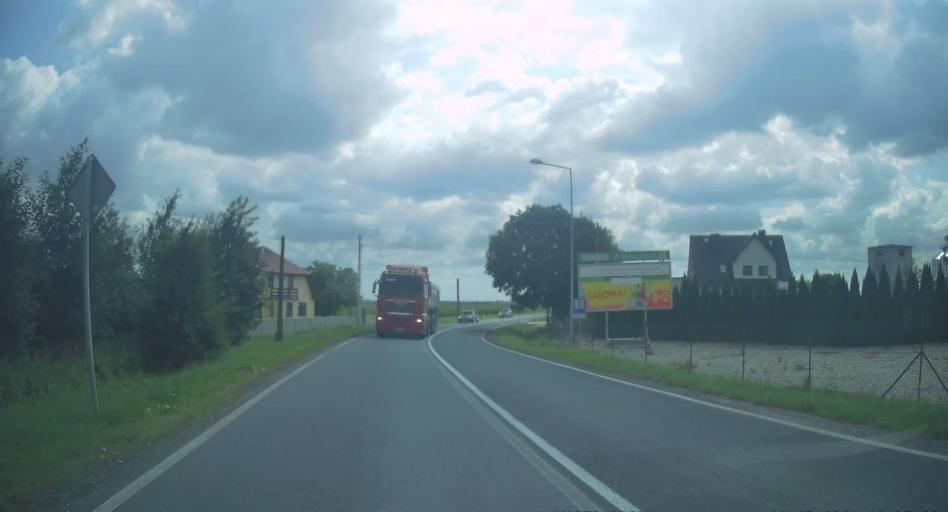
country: PL
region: Opole Voivodeship
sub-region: Powiat prudnicki
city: Glogowek
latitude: 50.3489
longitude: 17.8789
